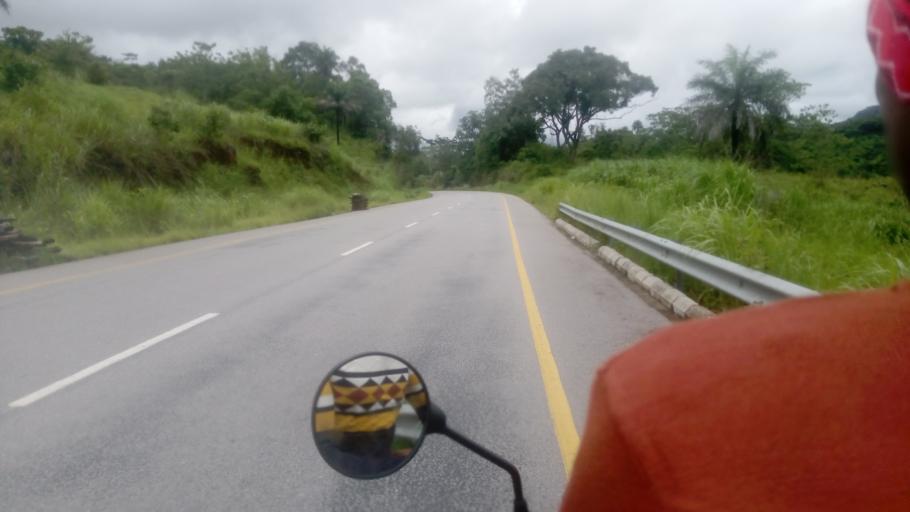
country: SL
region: Northern Province
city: Masaka
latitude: 8.6434
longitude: -11.7420
